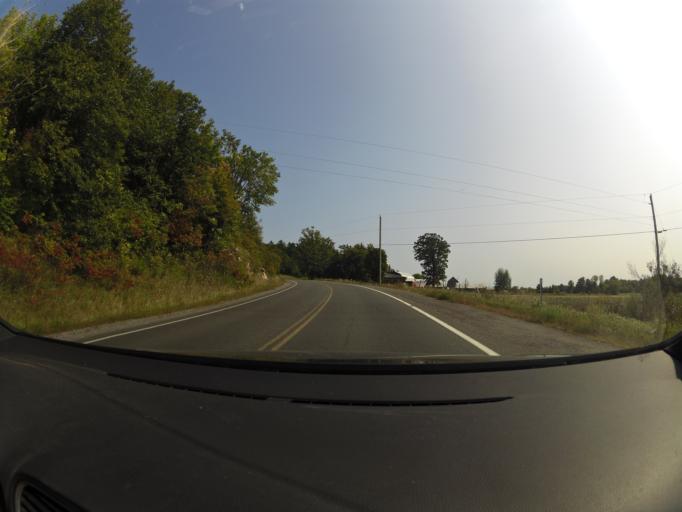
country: CA
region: Ontario
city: Carleton Place
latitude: 45.3654
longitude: -76.0816
